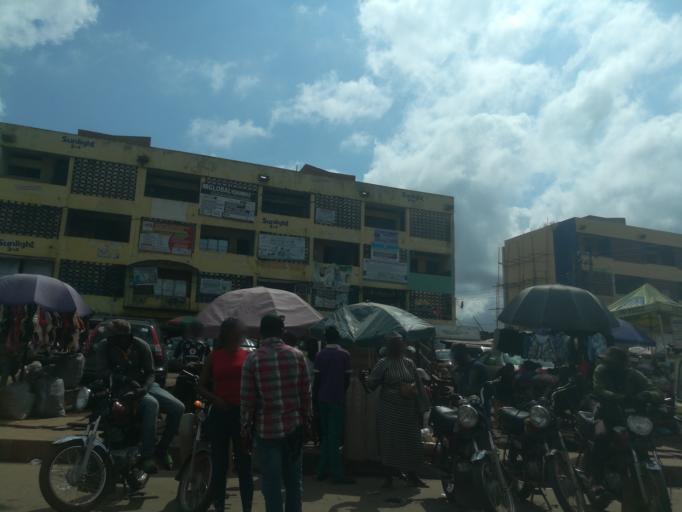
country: NG
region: Oyo
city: Ibadan
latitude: 7.3402
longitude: 3.8711
